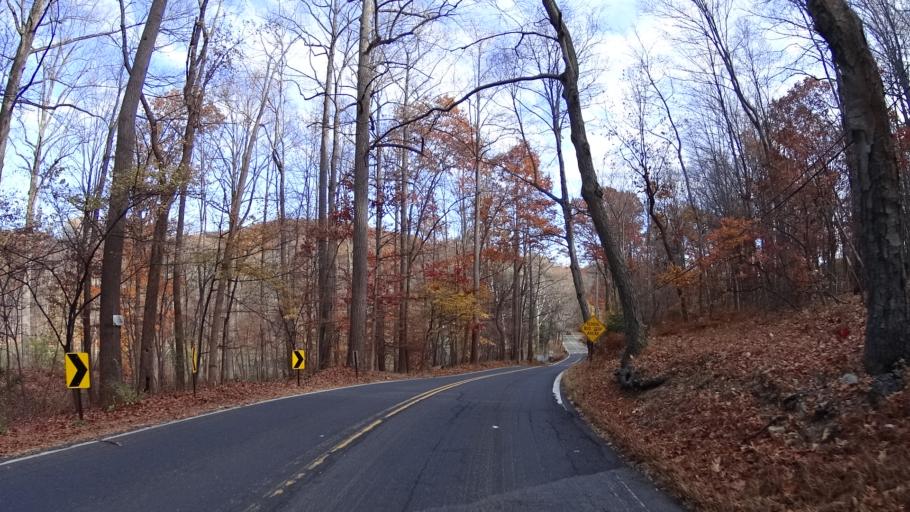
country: US
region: New Jersey
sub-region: Morris County
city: Mendham
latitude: 40.7668
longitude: -74.5564
